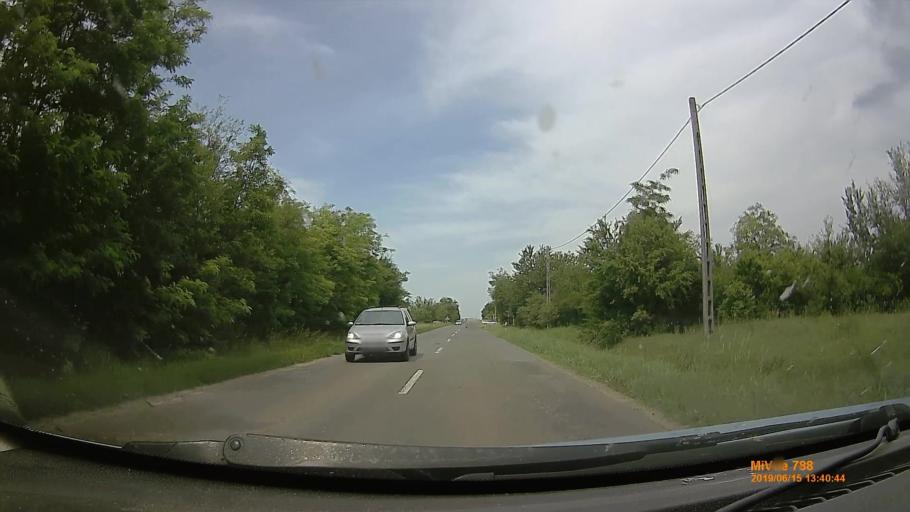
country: HU
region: Tolna
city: Iregszemcse
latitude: 46.6454
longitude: 18.1957
